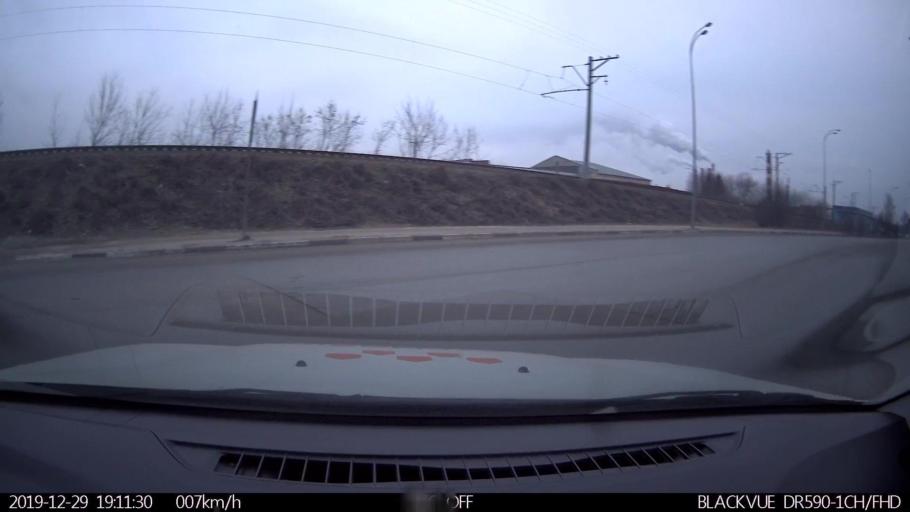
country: RU
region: Nizjnij Novgorod
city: Neklyudovo
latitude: 56.3551
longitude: 43.8672
